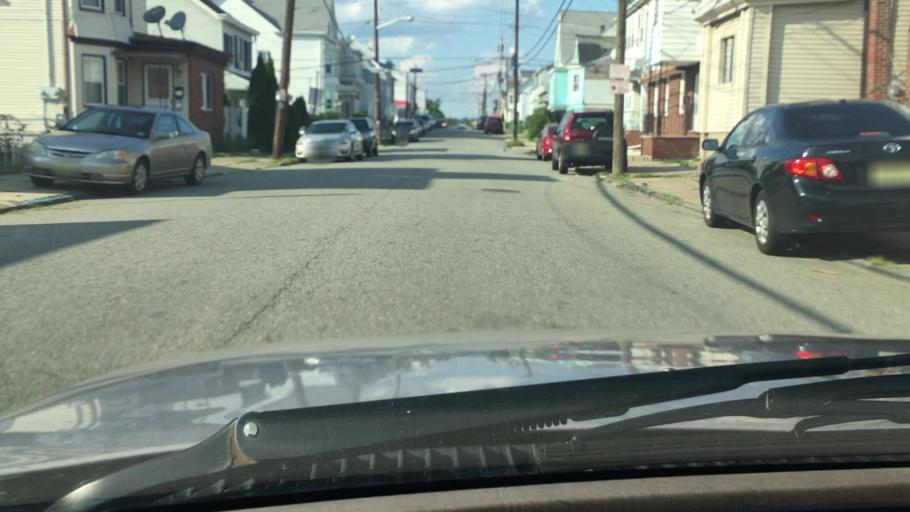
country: US
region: New Jersey
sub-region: Passaic County
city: Woodland Park
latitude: 40.9074
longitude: -74.1915
